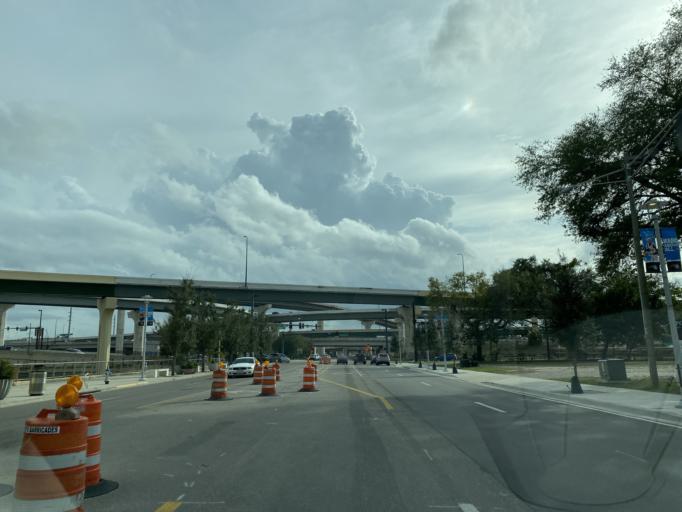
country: US
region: Florida
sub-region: Orange County
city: Orlando
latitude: 28.5374
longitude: -81.3849
